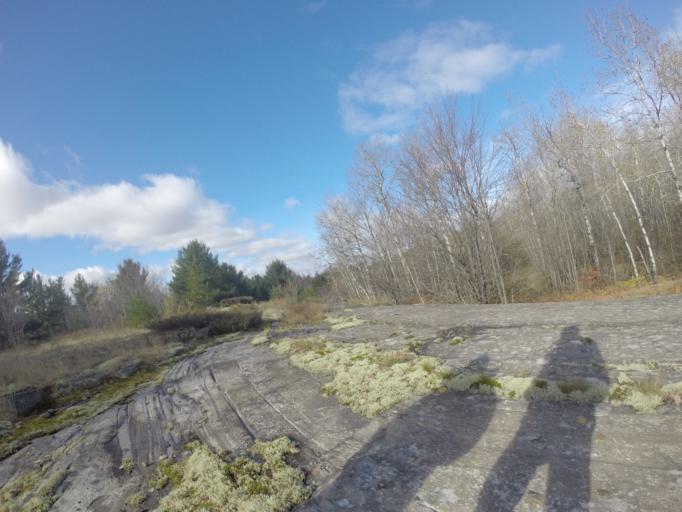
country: CA
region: Ontario
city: Greater Sudbury
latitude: 46.1084
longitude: -80.6510
